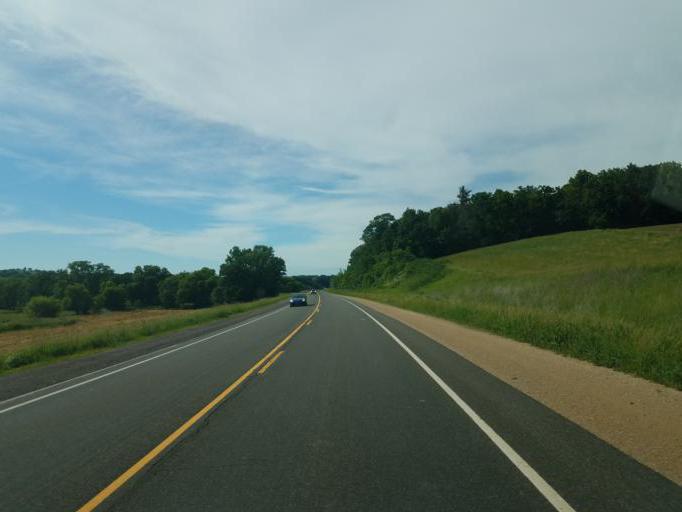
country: US
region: Wisconsin
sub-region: Monroe County
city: Tomah
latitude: 43.9197
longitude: -90.4962
